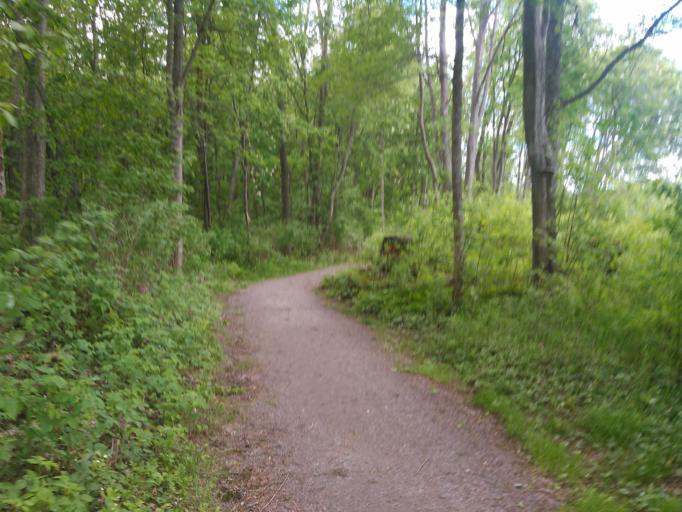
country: SE
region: Vaesterbotten
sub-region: Umea Kommun
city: Umea
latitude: 63.8253
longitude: 20.2391
